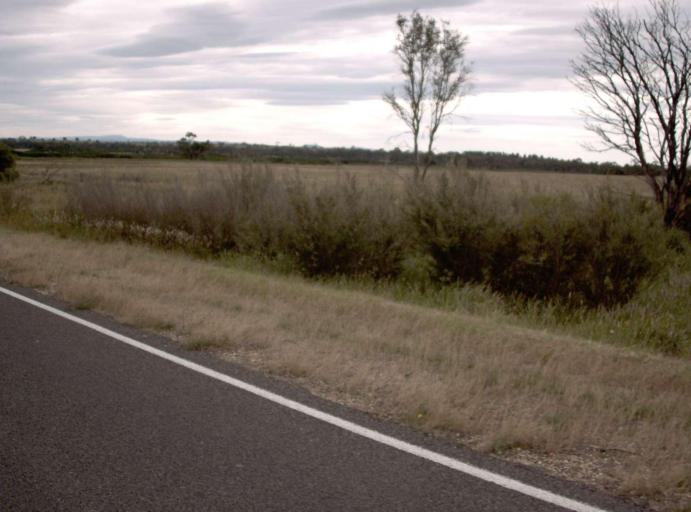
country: AU
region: Victoria
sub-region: East Gippsland
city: Bairnsdale
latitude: -37.9980
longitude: 147.3983
